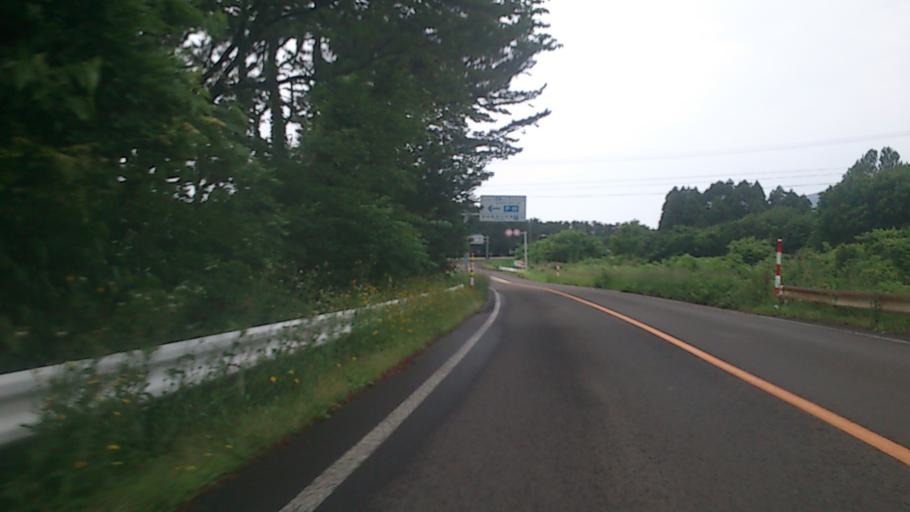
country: JP
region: Akita
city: Noshiromachi
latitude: 40.3887
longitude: 139.9839
